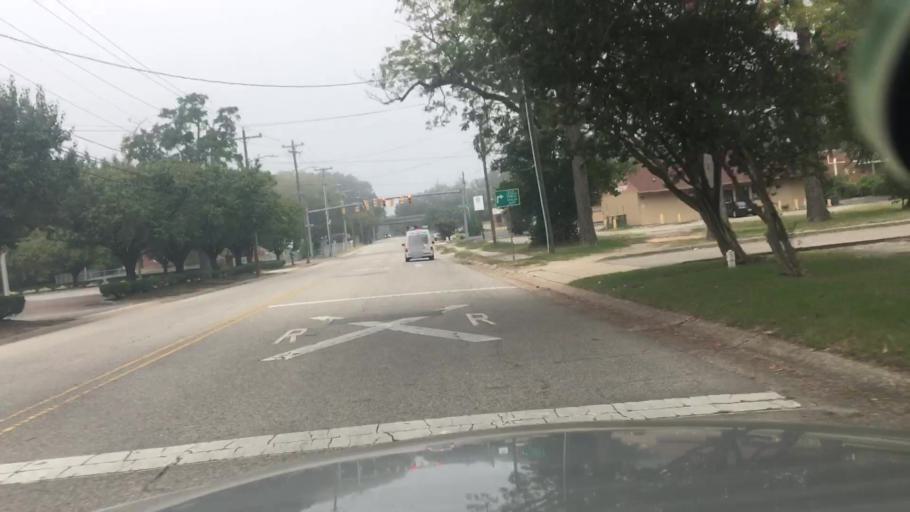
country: US
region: North Carolina
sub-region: Cumberland County
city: Fayetteville
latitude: 35.0658
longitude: -78.8828
